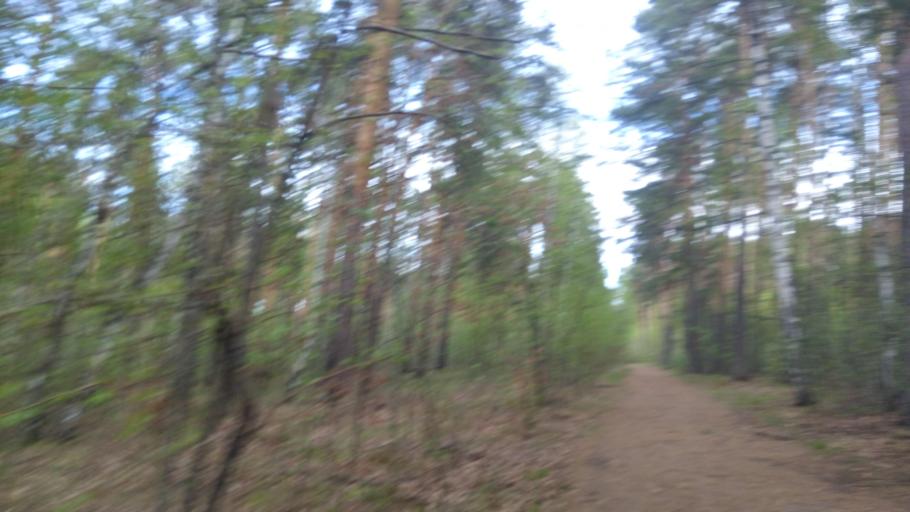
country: RU
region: Chelyabinsk
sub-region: Gorod Chelyabinsk
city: Chelyabinsk
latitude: 55.1624
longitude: 61.3480
